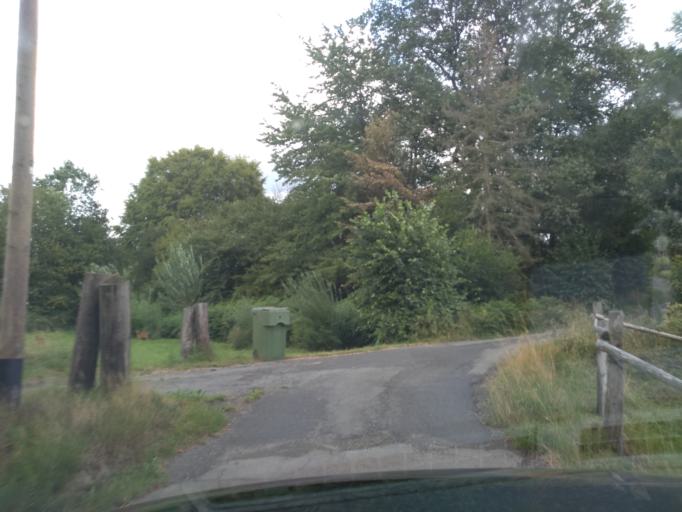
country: DE
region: North Rhine-Westphalia
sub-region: Regierungsbezirk Koln
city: Much
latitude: 50.9438
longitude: 7.4452
